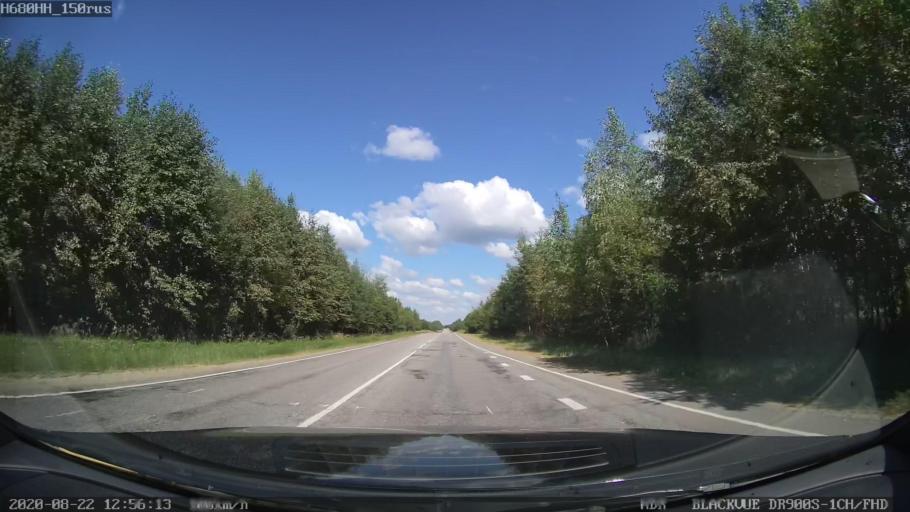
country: RU
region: Tverskaya
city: Rameshki
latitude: 57.5531
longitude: 36.3138
